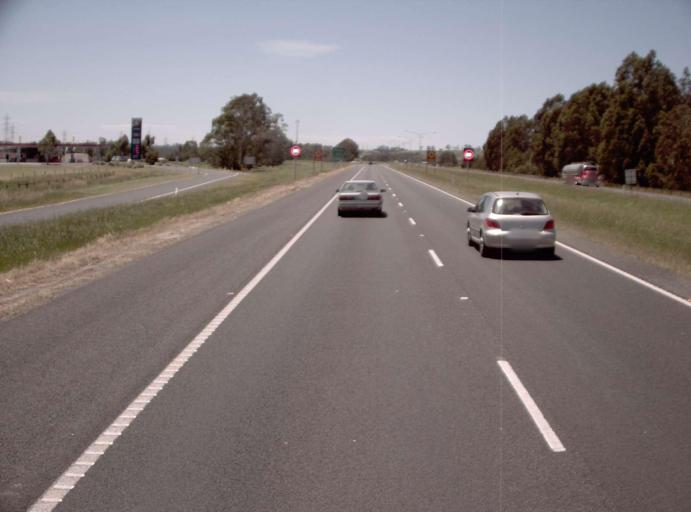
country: AU
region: Victoria
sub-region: Cardinia
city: Bunyip
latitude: -38.0861
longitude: 145.7719
